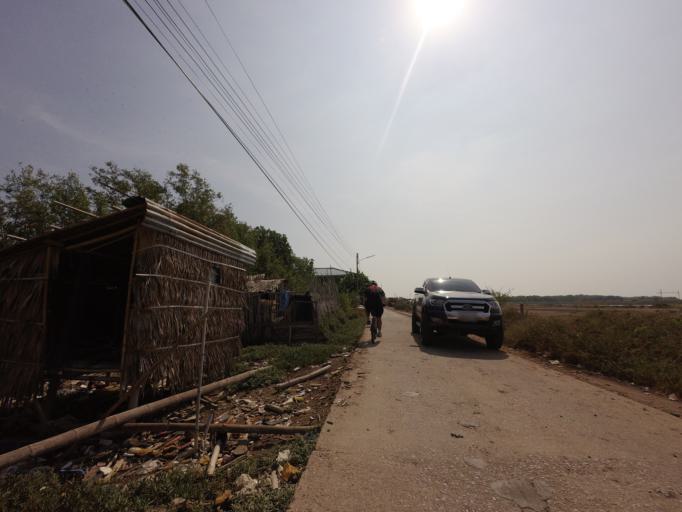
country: TH
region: Samut Sakhon
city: Samut Sakhon
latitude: 13.4964
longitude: 100.3861
